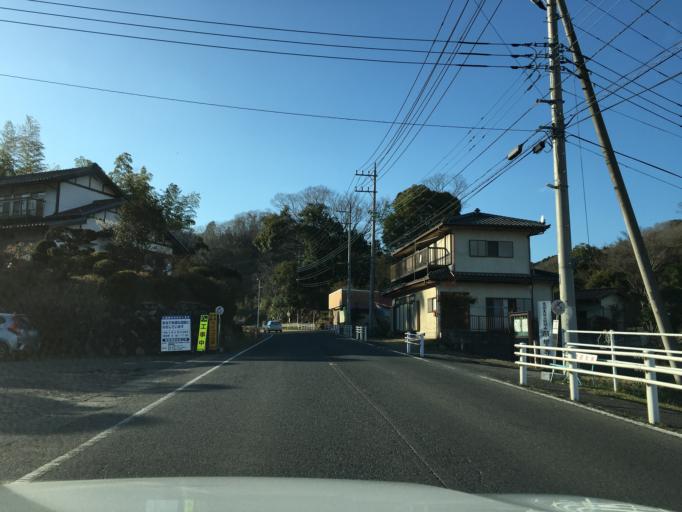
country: JP
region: Ibaraki
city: Daigo
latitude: 36.7784
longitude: 140.3427
